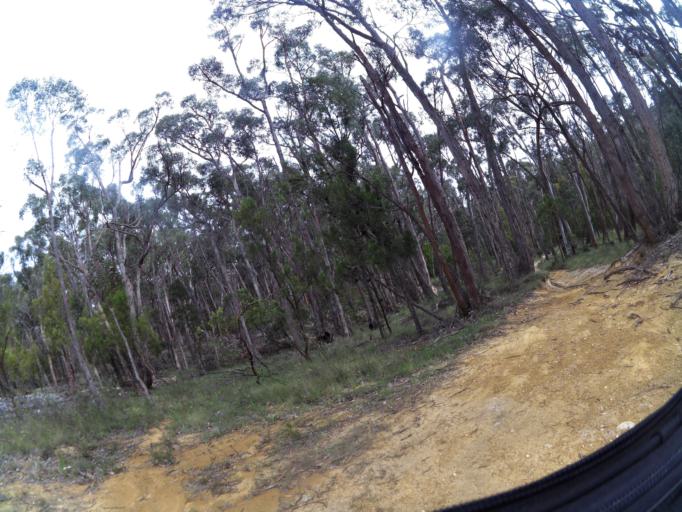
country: AU
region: Victoria
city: Brown Hill
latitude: -37.4703
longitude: 143.9098
